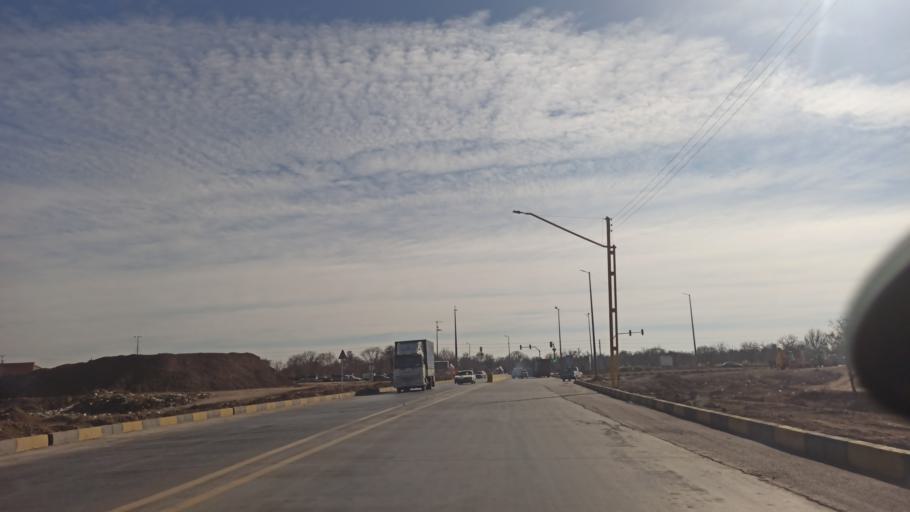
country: IR
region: Qazvin
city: Qazvin
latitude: 36.2573
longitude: 49.9779
